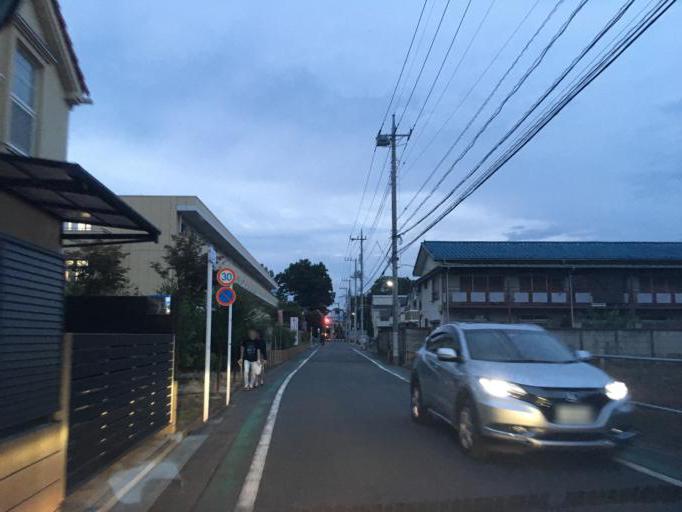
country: JP
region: Tokyo
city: Kokubunji
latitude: 35.7211
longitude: 139.4567
